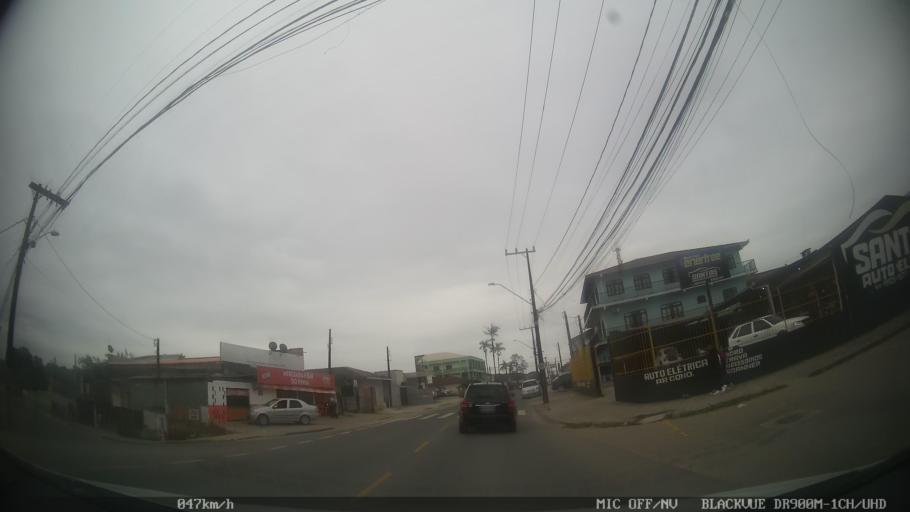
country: BR
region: Santa Catarina
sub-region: Joinville
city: Joinville
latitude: -26.3306
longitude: -48.8174
